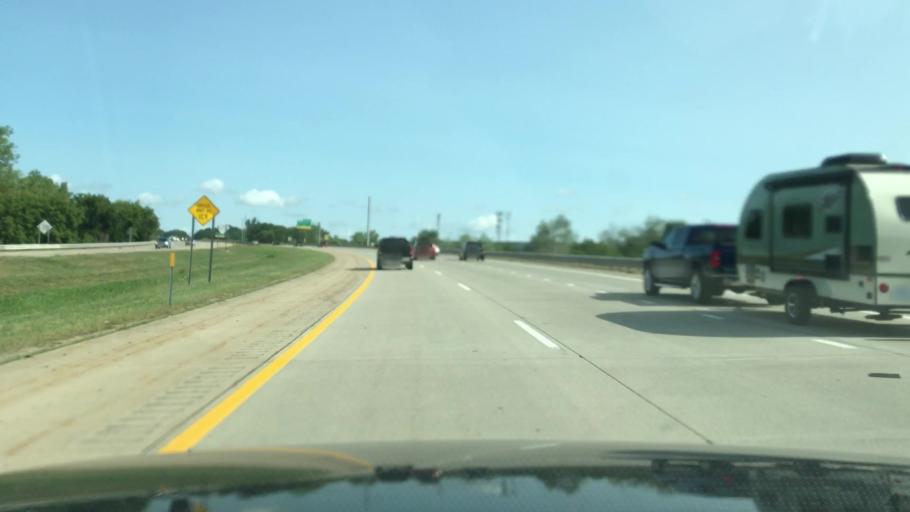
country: US
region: Michigan
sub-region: Kent County
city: Comstock Park
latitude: 43.0370
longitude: -85.6615
